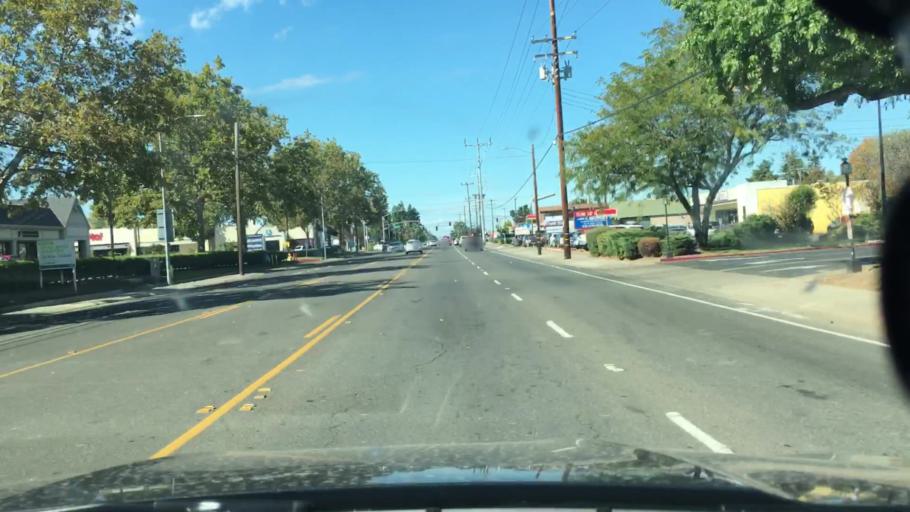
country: US
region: California
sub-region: Sacramento County
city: Arden-Arcade
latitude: 38.5959
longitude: -121.3894
